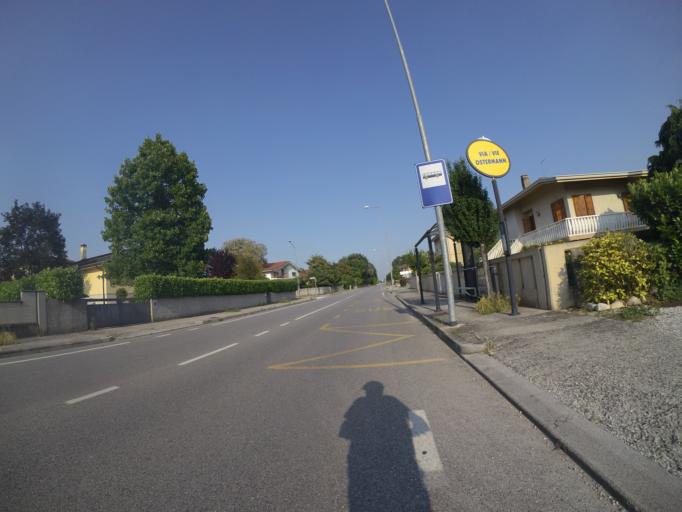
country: IT
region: Friuli Venezia Giulia
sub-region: Provincia di Udine
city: Codroipo
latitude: 45.9590
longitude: 12.9924
